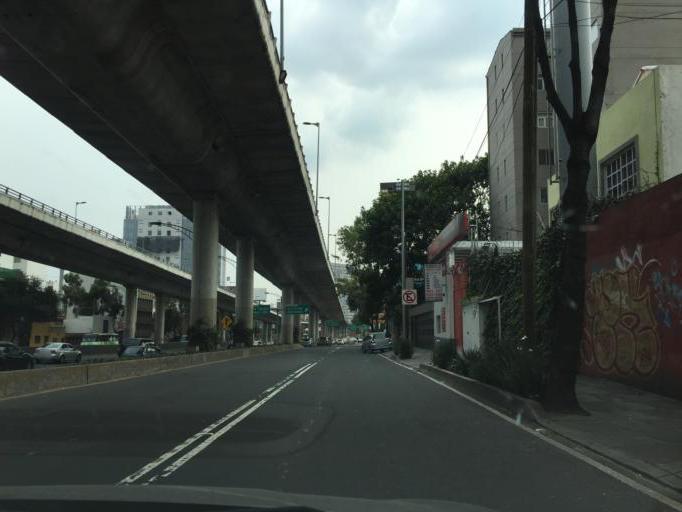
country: MX
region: Mexico City
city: Alvaro Obregon
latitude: 19.3664
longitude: -99.1910
